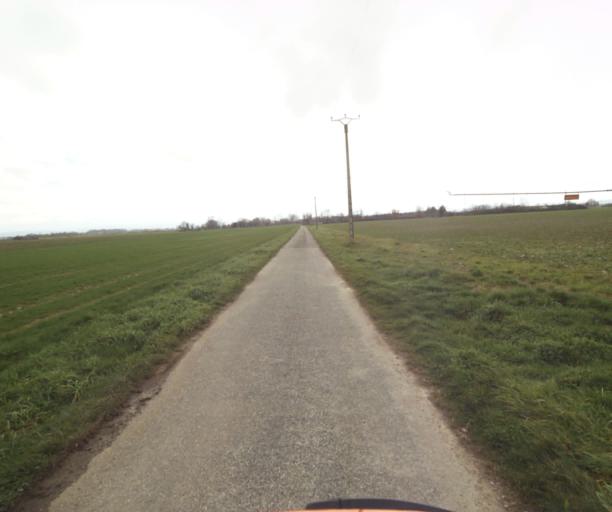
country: FR
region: Midi-Pyrenees
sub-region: Departement de l'Ariege
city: La Tour-du-Crieu
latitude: 43.1666
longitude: 1.6849
